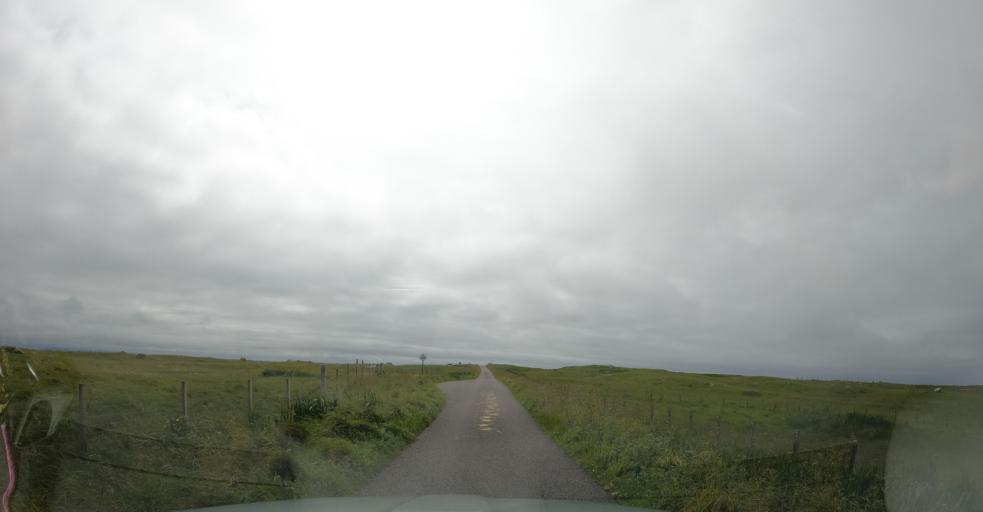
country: GB
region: Scotland
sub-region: Eilean Siar
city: Isle of North Uist
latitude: 57.5327
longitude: -7.3549
